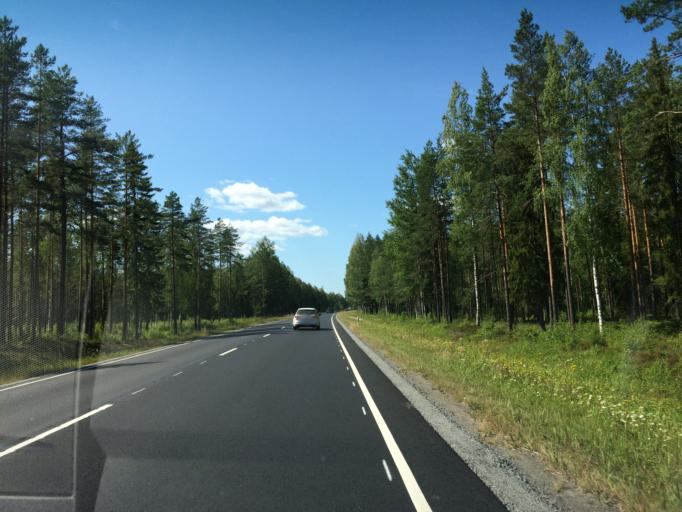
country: FI
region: Pirkanmaa
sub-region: Lounais-Pirkanmaa
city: Kiikoinen
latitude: 61.4732
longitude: 22.5239
